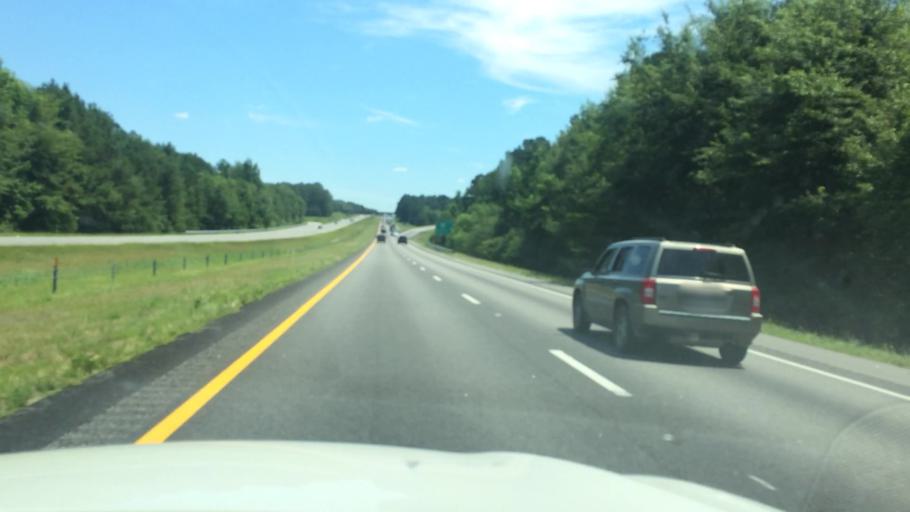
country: US
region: South Carolina
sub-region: Lexington County
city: Leesville
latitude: 33.8104
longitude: -81.4581
